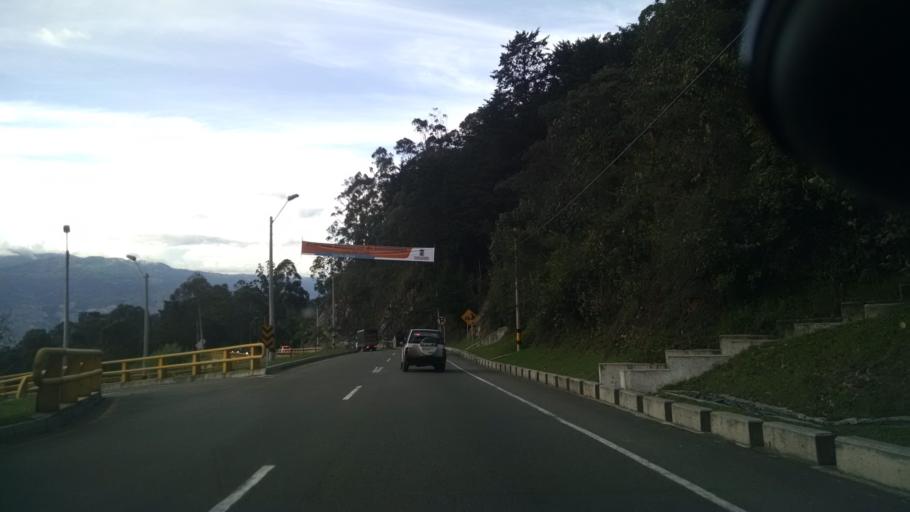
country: CO
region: Antioquia
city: Medellin
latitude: 6.2025
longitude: -75.5439
